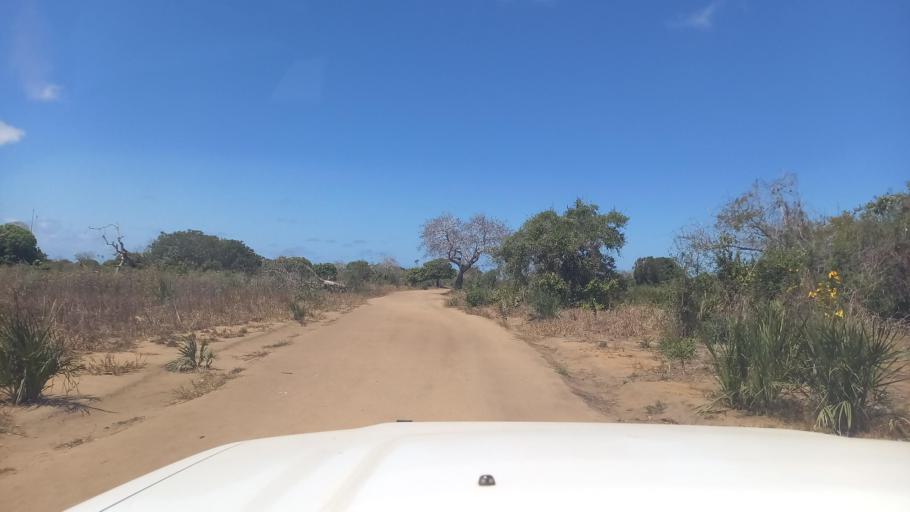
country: MZ
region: Cabo Delgado
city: Pemba
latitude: -13.4216
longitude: 40.5087
